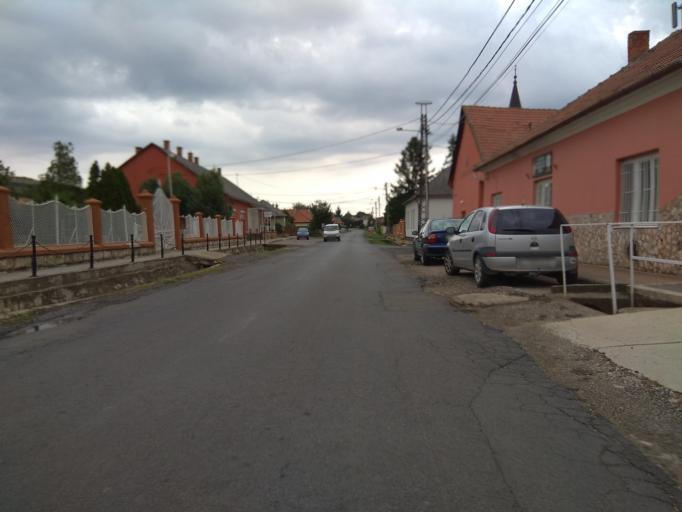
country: HU
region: Borsod-Abauj-Zemplen
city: Bekecs
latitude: 48.1589
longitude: 21.1530
